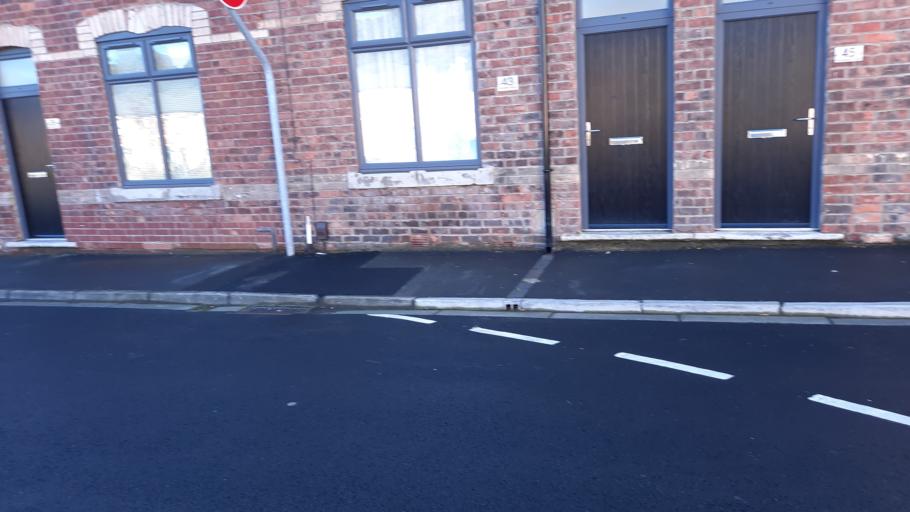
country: GB
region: England
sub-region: Hartlepool
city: Hartlepool
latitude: 54.6897
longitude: -1.2218
